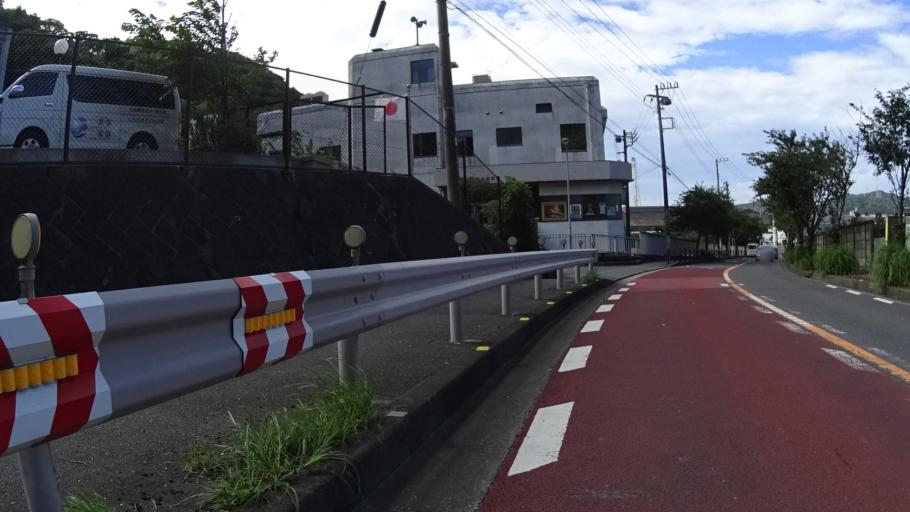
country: JP
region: Kanagawa
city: Yokosuka
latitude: 35.2302
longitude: 139.7232
